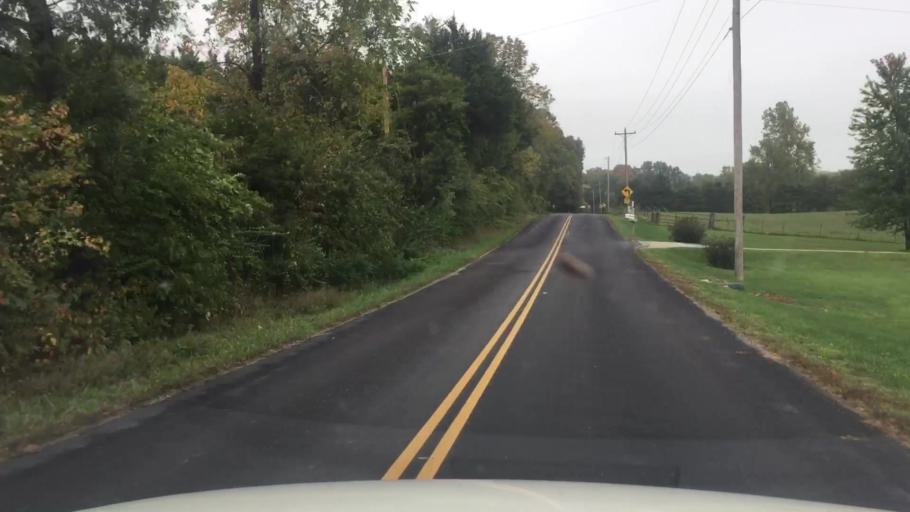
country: US
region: Missouri
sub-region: Boone County
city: Ashland
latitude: 38.8169
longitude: -92.2928
